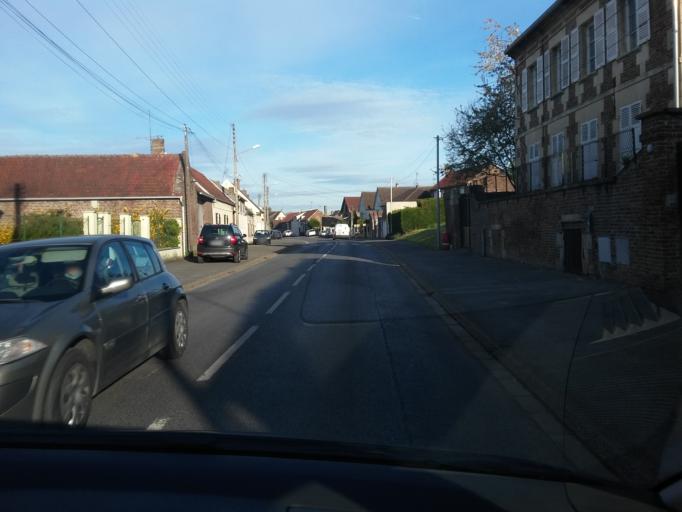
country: FR
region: Picardie
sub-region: Departement de l'Oise
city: Chevrieres
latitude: 49.3473
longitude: 2.6918
